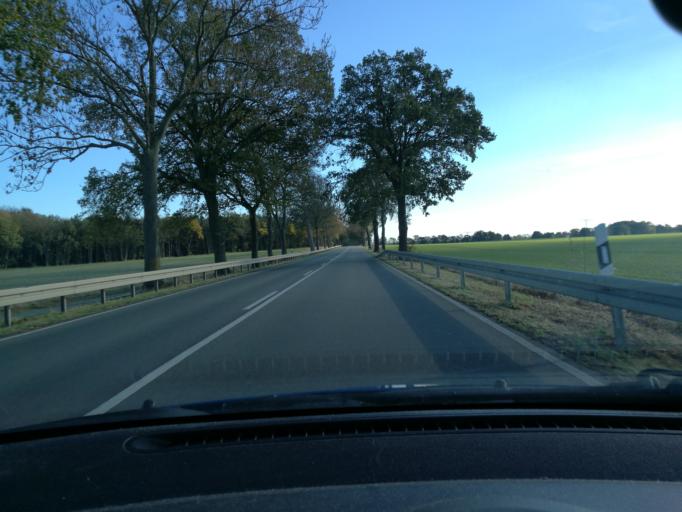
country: DE
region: Brandenburg
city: Perleberg
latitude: 53.1126
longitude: 11.8182
